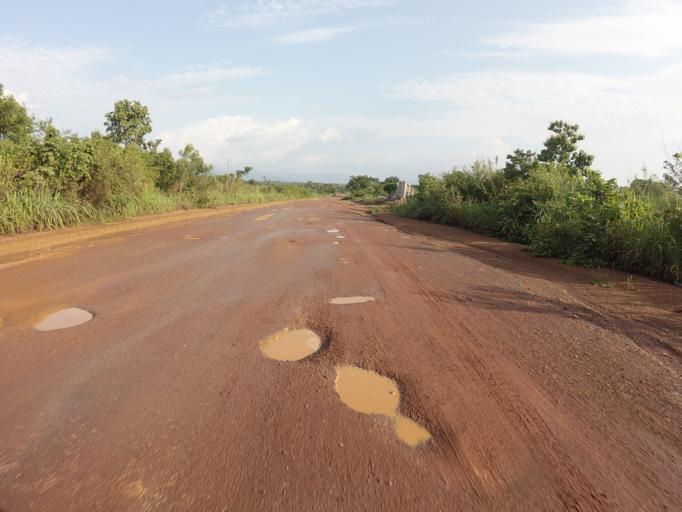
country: GH
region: Volta
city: Kpandu
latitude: 7.0175
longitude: 0.4282
